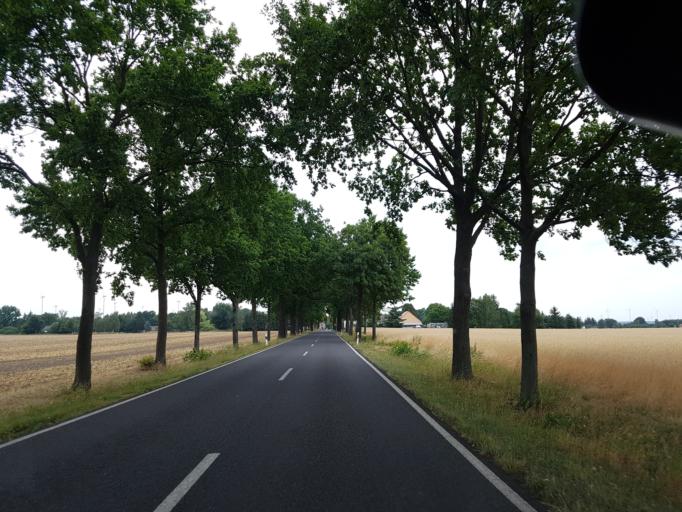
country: DE
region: Brandenburg
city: Sallgast
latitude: 51.6047
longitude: 13.8450
